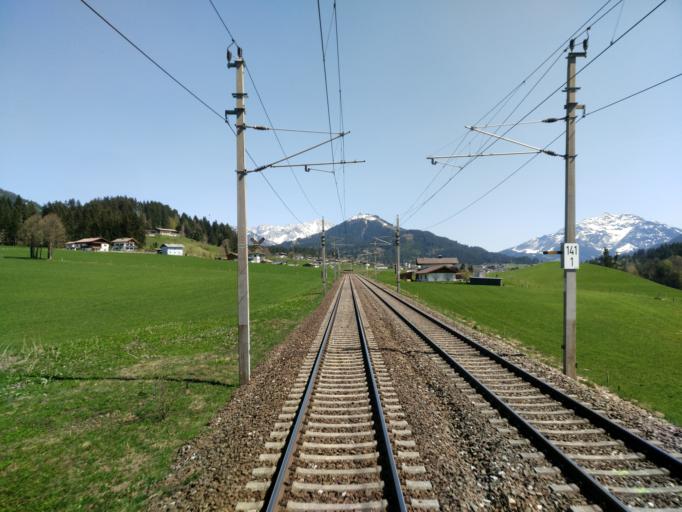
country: AT
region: Tyrol
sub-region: Politischer Bezirk Kitzbuhel
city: Fieberbrunn
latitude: 47.4956
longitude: 12.5070
